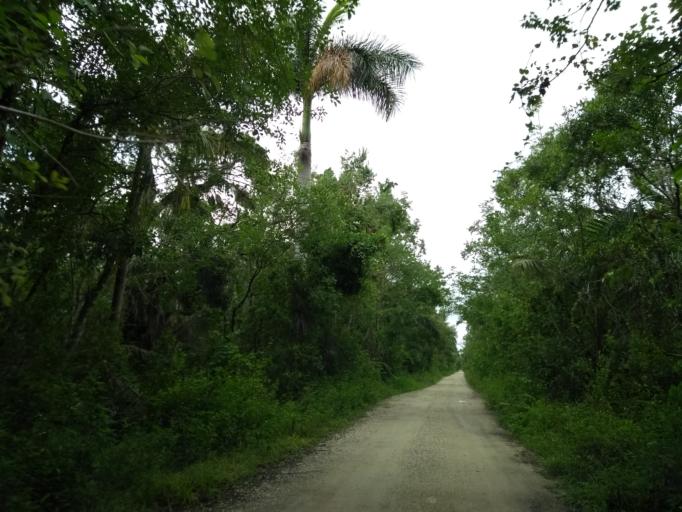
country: US
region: Florida
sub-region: Collier County
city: Lely Resort
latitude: 25.9991
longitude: -81.4111
